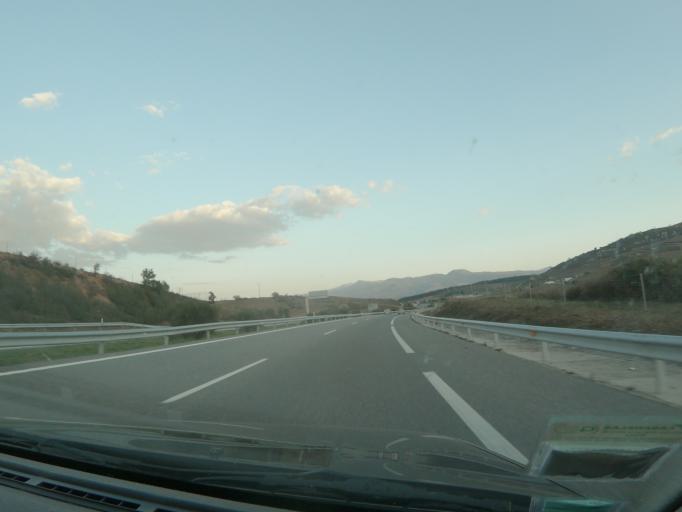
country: ES
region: Castille and Leon
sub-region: Provincia de Leon
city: Villadecanes
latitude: 42.5827
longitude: -6.7849
